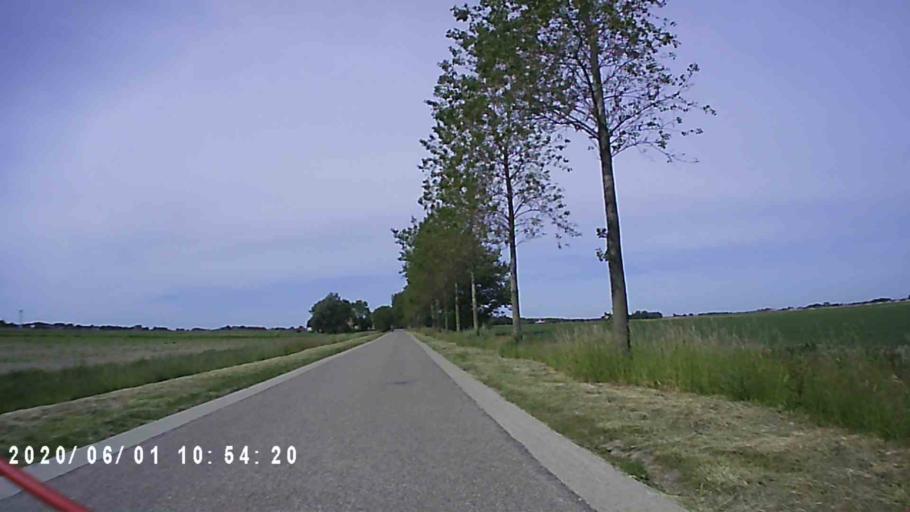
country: NL
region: Friesland
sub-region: Gemeente Franekeradeel
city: Sexbierum
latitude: 53.2008
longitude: 5.5118
